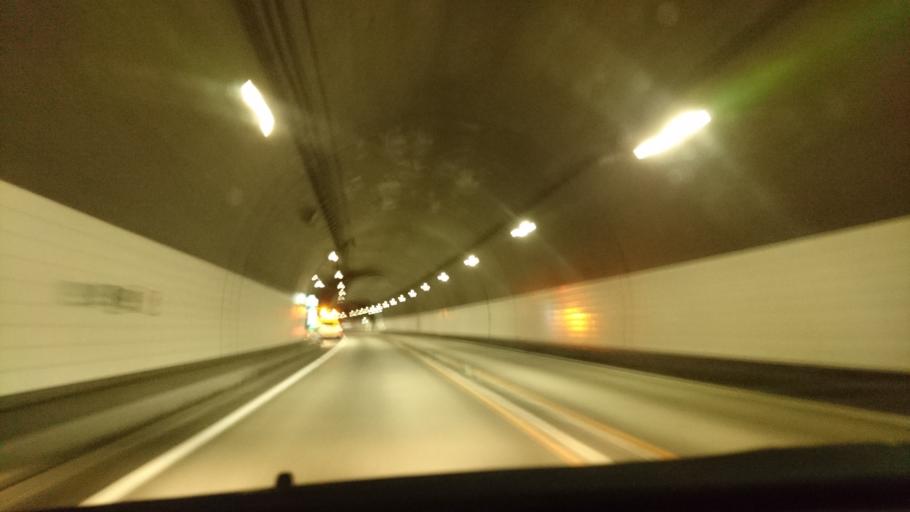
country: JP
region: Iwate
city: Tono
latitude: 39.2440
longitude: 141.6379
